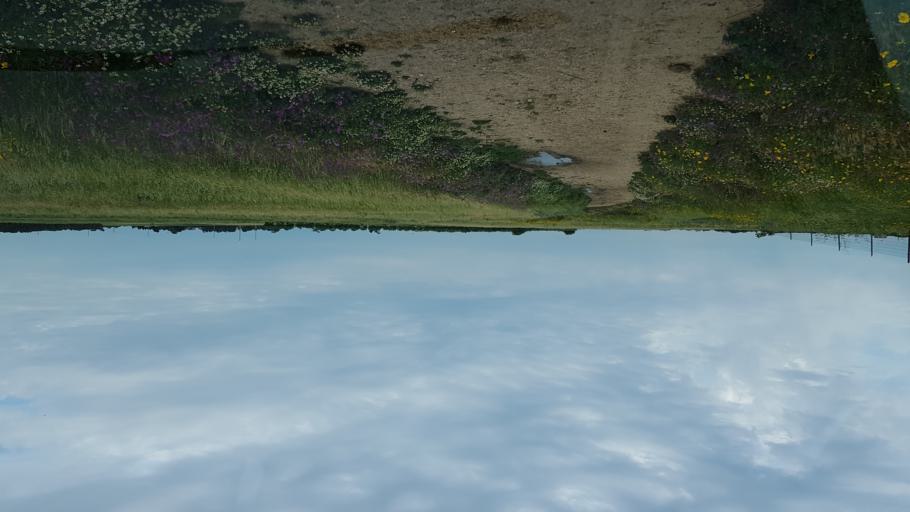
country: IT
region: Apulia
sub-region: Provincia di Brindisi
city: Brindisi
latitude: 40.6547
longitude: 17.8698
